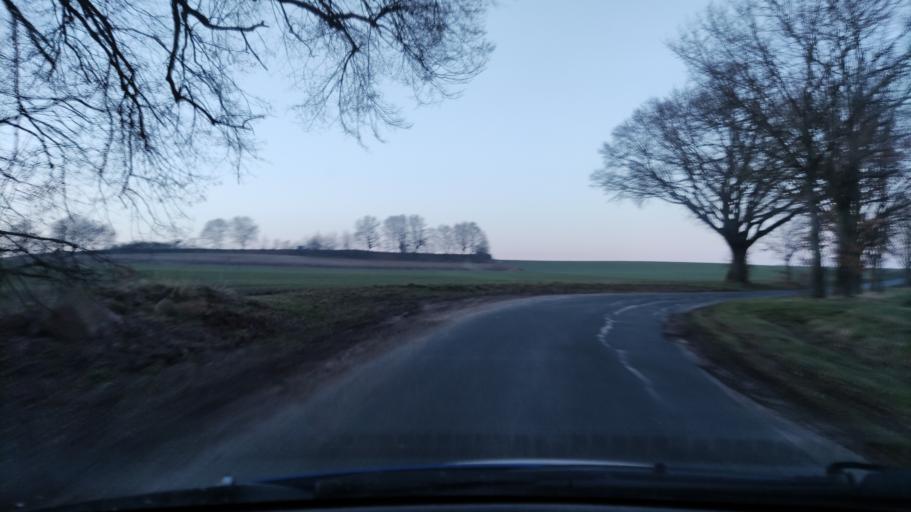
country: DE
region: Lower Saxony
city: Natendorf
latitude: 53.0480
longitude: 10.4782
